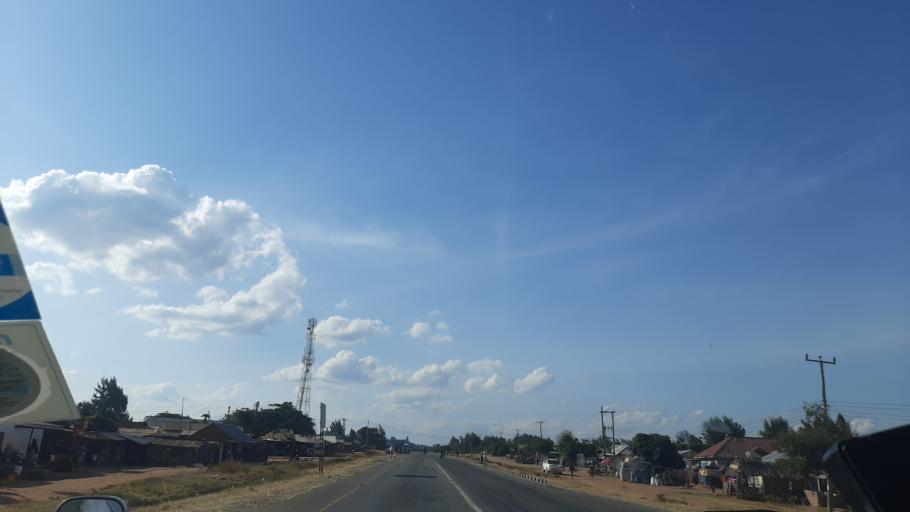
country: TZ
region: Singida
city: Puma
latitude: -5.0053
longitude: 34.7574
